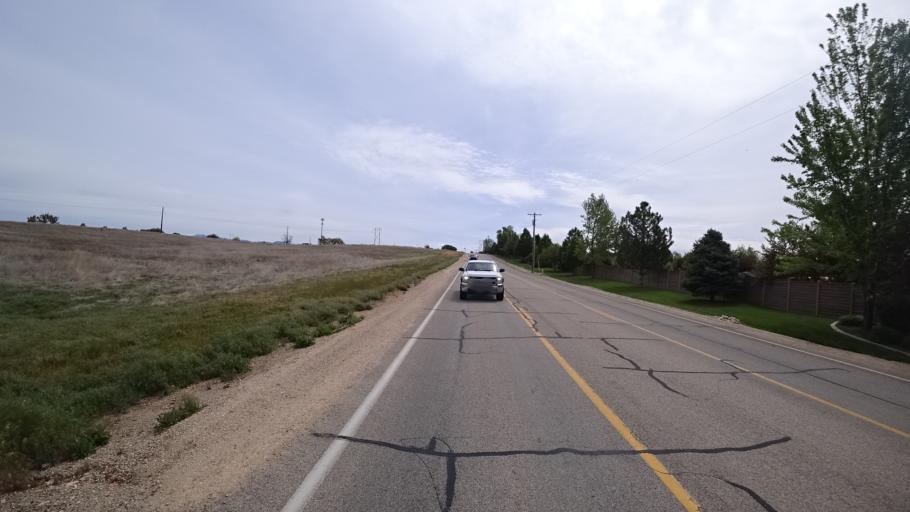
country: US
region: Idaho
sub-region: Ada County
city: Meridian
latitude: 43.5612
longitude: -116.4425
